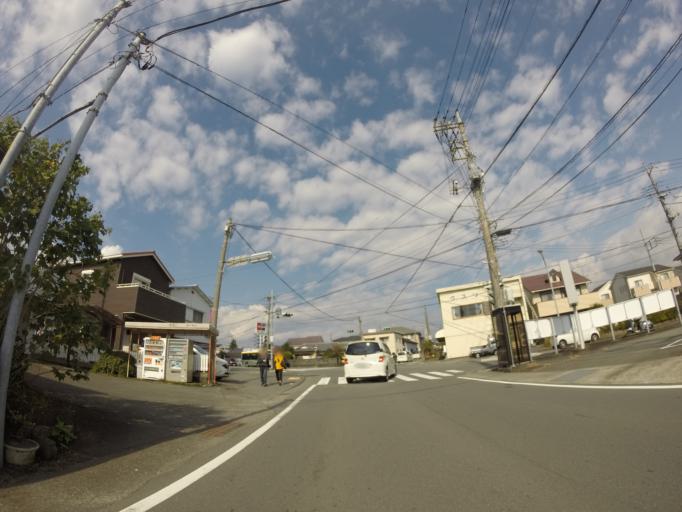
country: JP
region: Shizuoka
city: Fujinomiya
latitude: 35.2164
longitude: 138.6261
